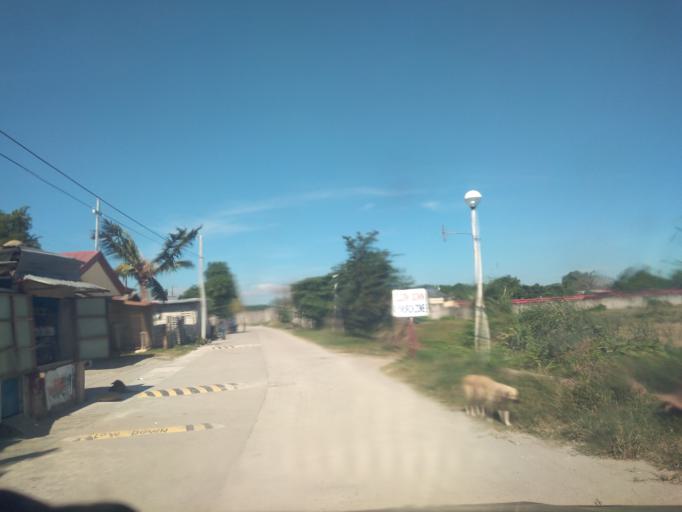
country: PH
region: Central Luzon
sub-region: Province of Pampanga
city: Calibutbut
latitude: 15.0916
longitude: 120.5963
